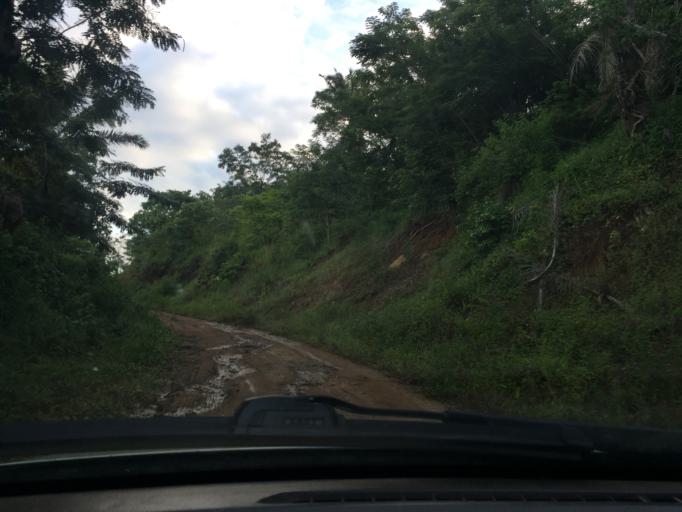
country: TZ
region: Tanga
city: Muheza
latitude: -5.1313
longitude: 38.7703
